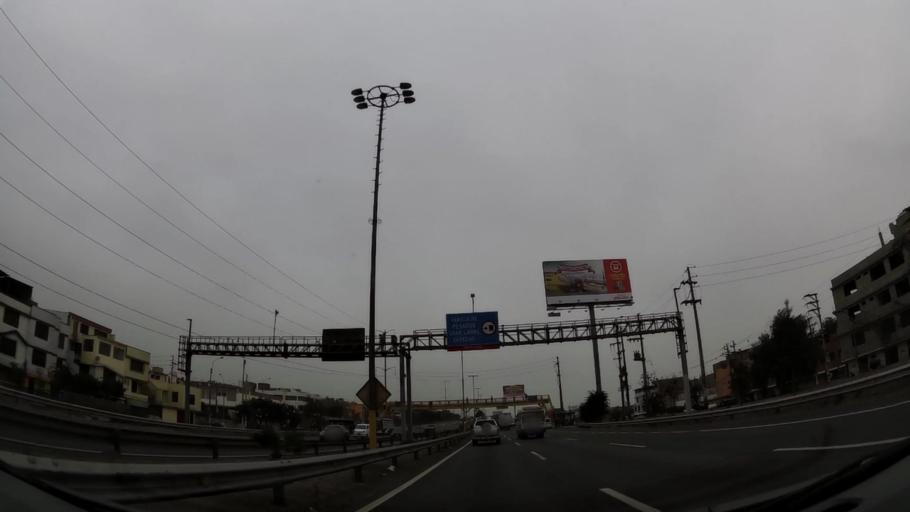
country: PE
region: Lima
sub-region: Lima
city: Surco
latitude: -12.1612
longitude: -76.9821
